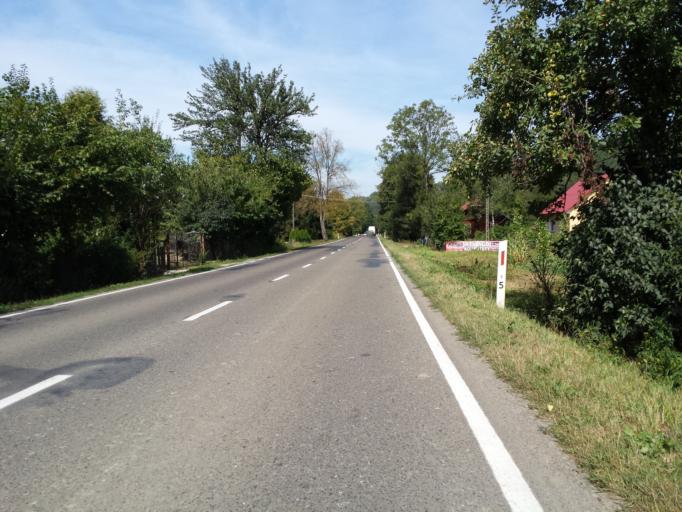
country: PL
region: Subcarpathian Voivodeship
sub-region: Powiat leski
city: Lesko
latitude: 49.4512
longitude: 22.3451
